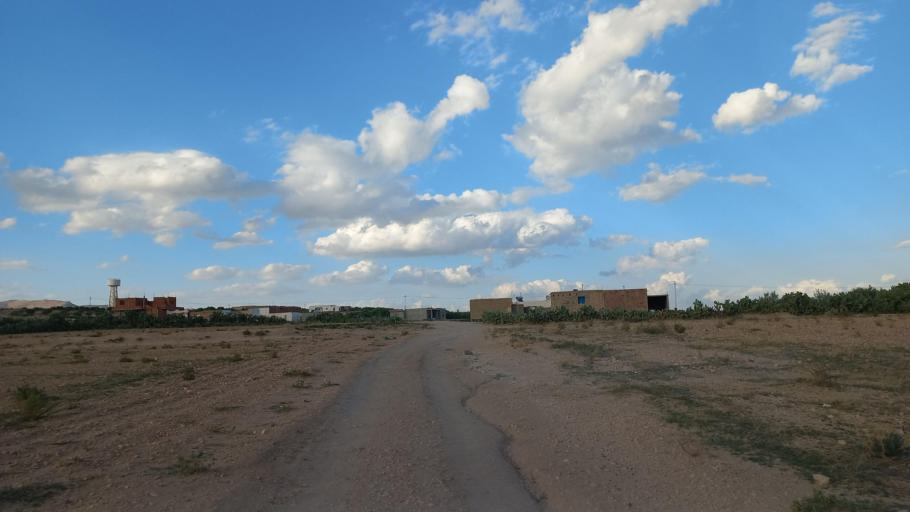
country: TN
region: Al Qasrayn
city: Sbiba
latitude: 35.3862
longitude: 9.0454
